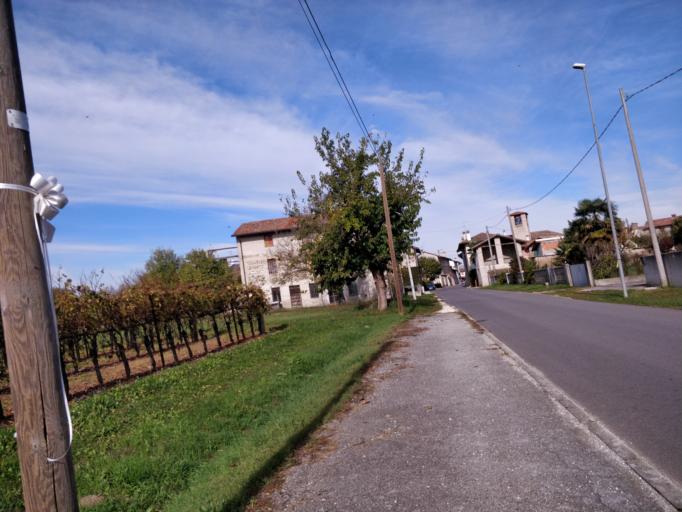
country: IT
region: Friuli Venezia Giulia
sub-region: Provincia di Udine
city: Bertiolo
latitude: 45.9419
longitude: 13.0247
